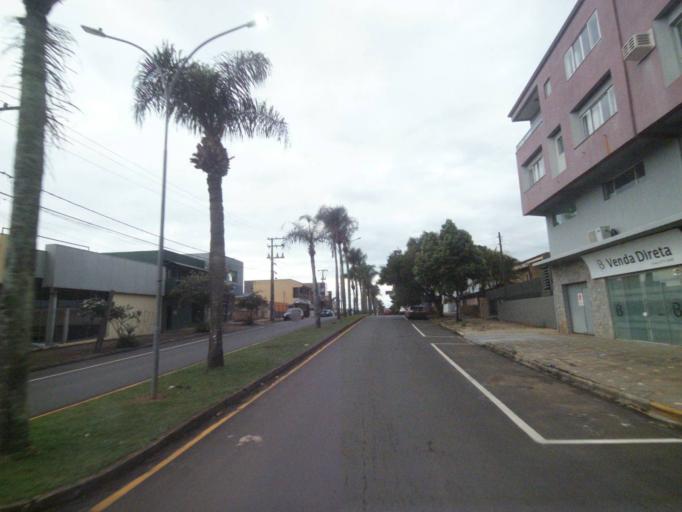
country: BR
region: Parana
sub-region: Telemaco Borba
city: Telemaco Borba
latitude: -24.3297
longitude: -50.6241
